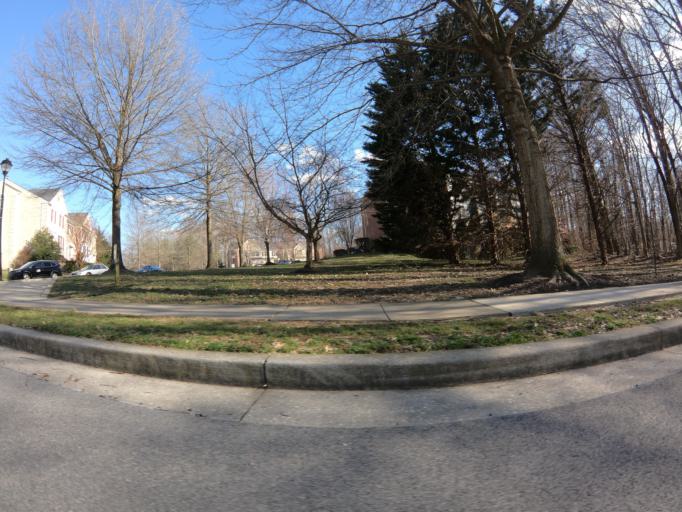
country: US
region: Maryland
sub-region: Howard County
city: Ellicott City
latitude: 39.2572
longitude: -76.8025
